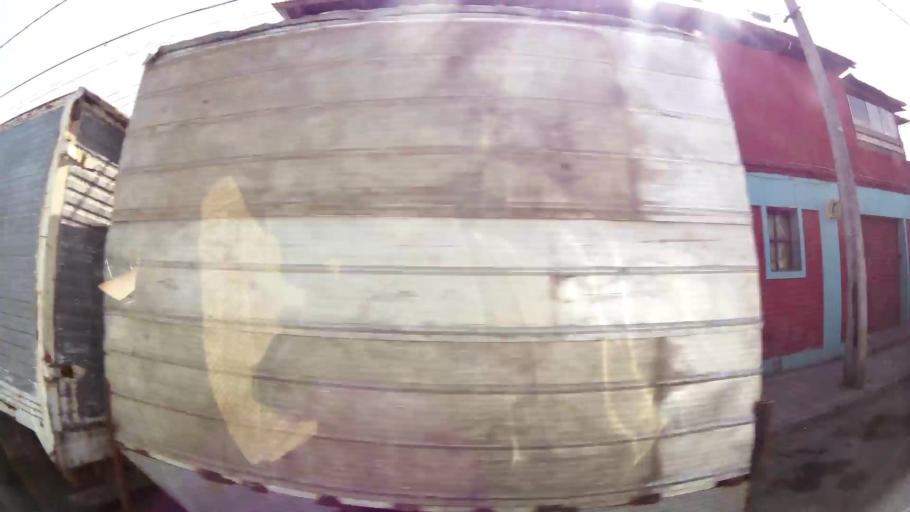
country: CL
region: Santiago Metropolitan
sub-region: Provincia de Santiago
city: Lo Prado
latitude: -33.4343
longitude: -70.7654
